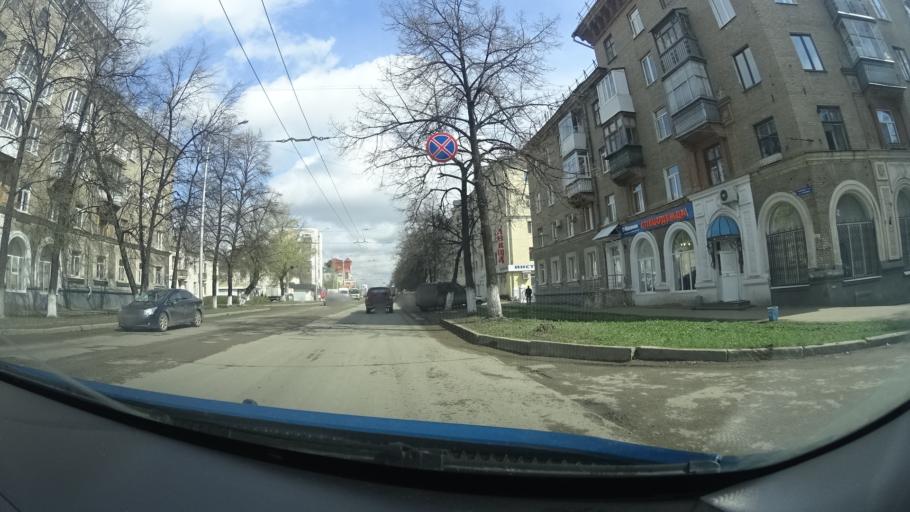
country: RU
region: Bashkortostan
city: Ufa
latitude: 54.8204
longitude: 56.0773
